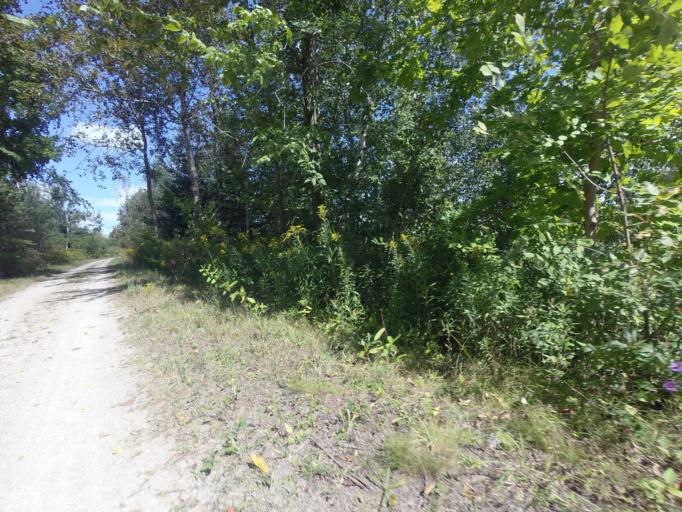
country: CA
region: Ontario
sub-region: Wellington County
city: Guelph
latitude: 43.7622
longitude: -80.3250
